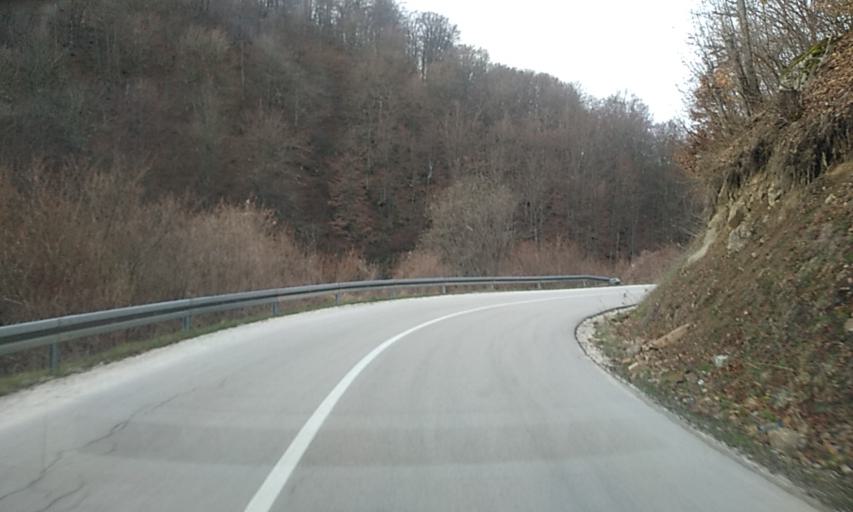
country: RS
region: Central Serbia
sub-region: Pcinjski Okrug
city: Bosilegrad
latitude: 42.5792
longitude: 22.4083
